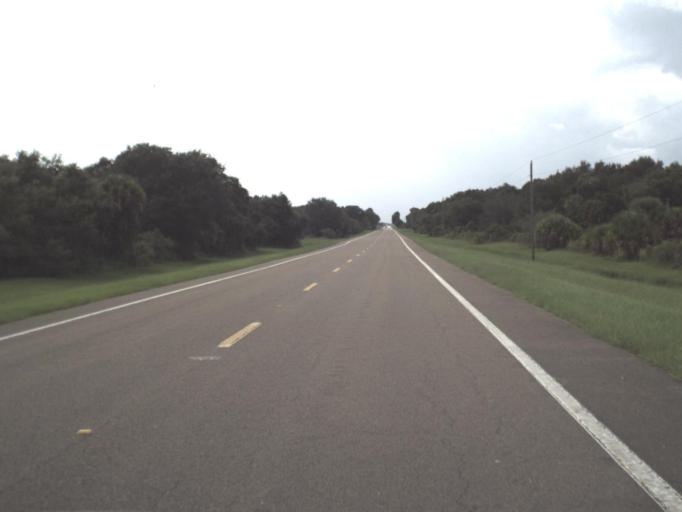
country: US
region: Florida
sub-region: Sarasota County
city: North Port
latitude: 27.1934
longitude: -82.1453
